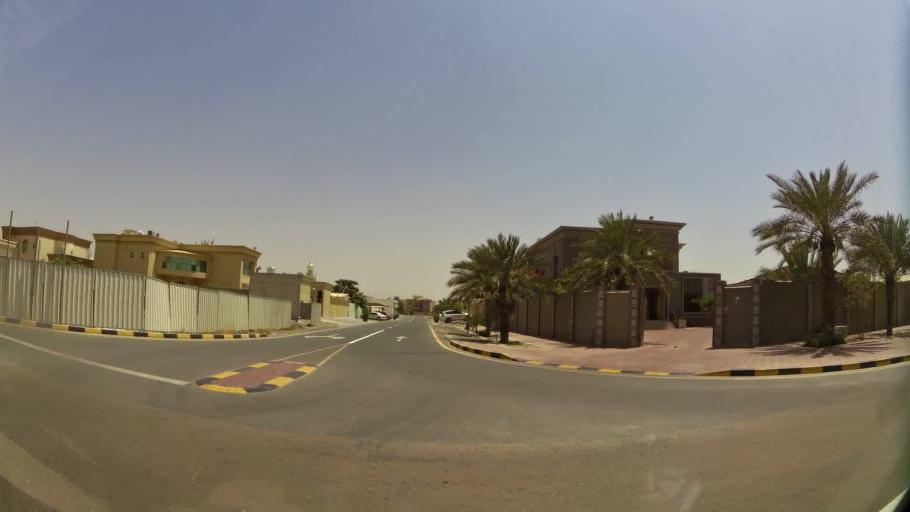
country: AE
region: Ajman
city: Ajman
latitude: 25.4269
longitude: 55.5181
